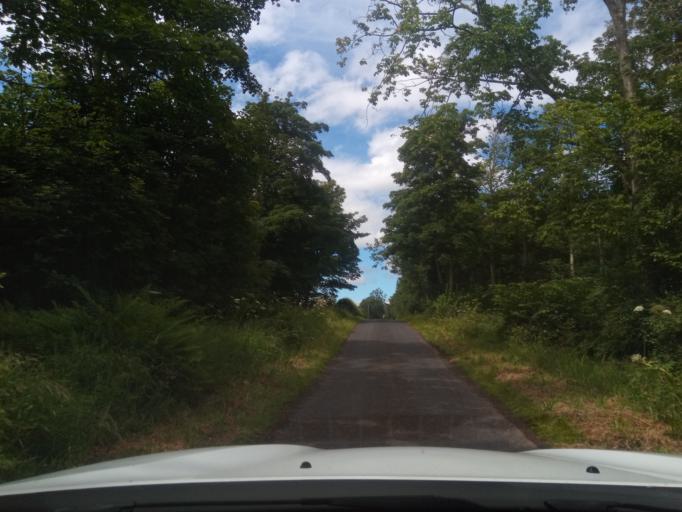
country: GB
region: Scotland
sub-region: The Scottish Borders
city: Jedburgh
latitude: 55.5611
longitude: -2.5351
